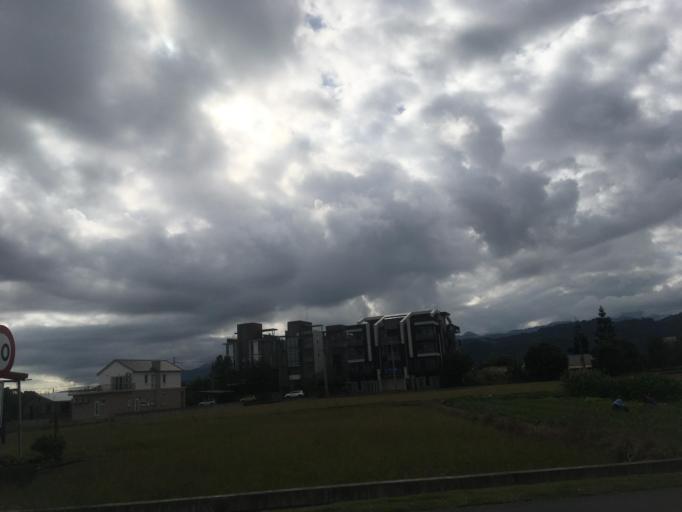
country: TW
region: Taiwan
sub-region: Yilan
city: Yilan
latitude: 24.6819
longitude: 121.6897
